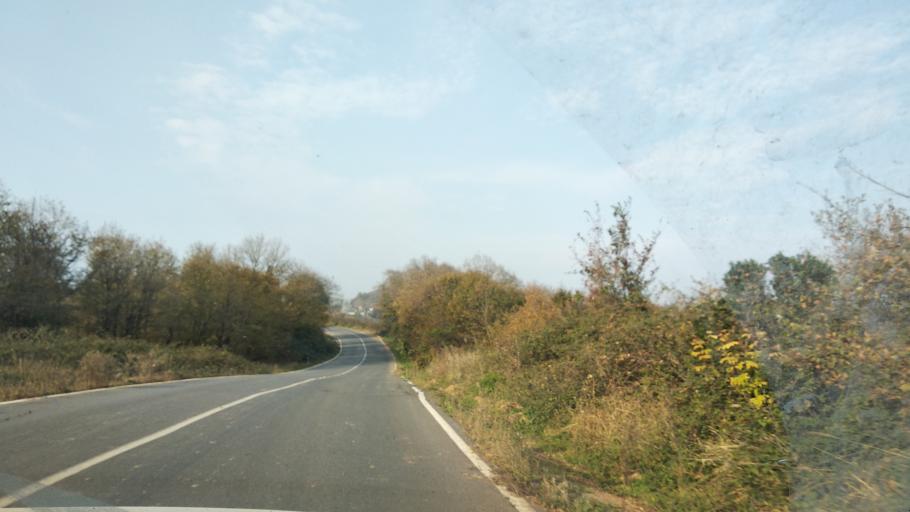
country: TR
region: Sakarya
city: Karasu
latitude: 41.0669
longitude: 30.6160
